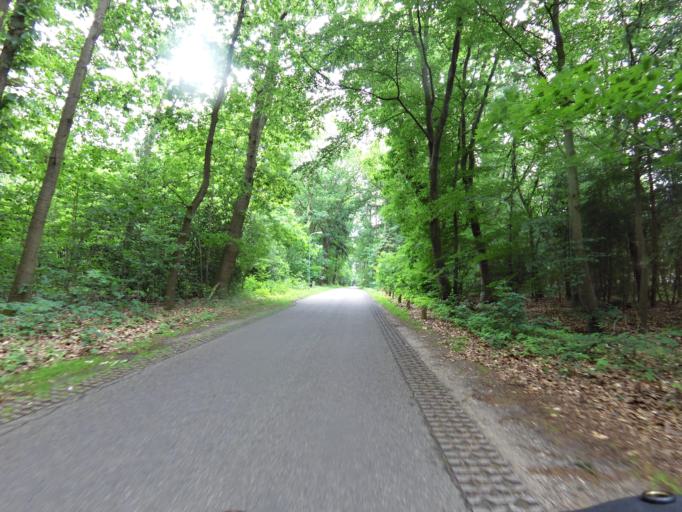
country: NL
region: Gelderland
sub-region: Gemeente Apeldoorn
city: Uddel
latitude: 52.2873
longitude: 5.7956
